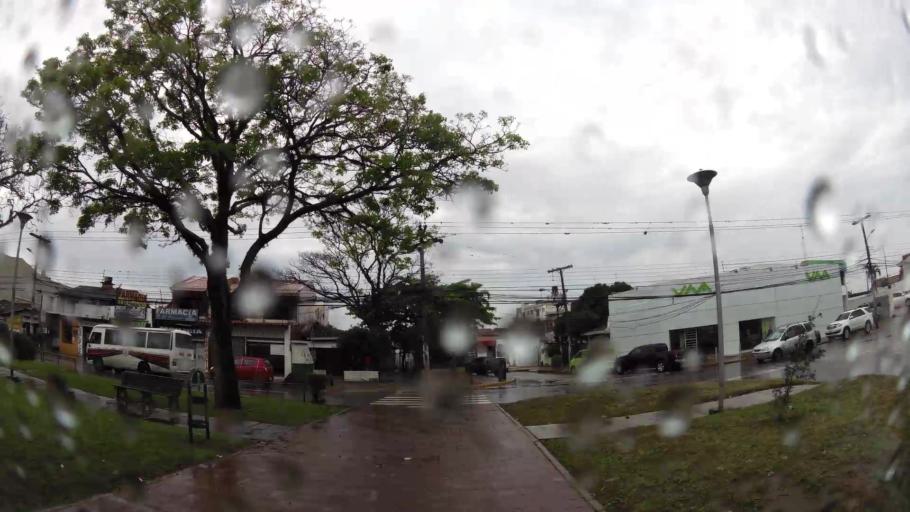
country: BO
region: Santa Cruz
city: Santa Cruz de la Sierra
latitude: -17.7900
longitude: -63.1717
